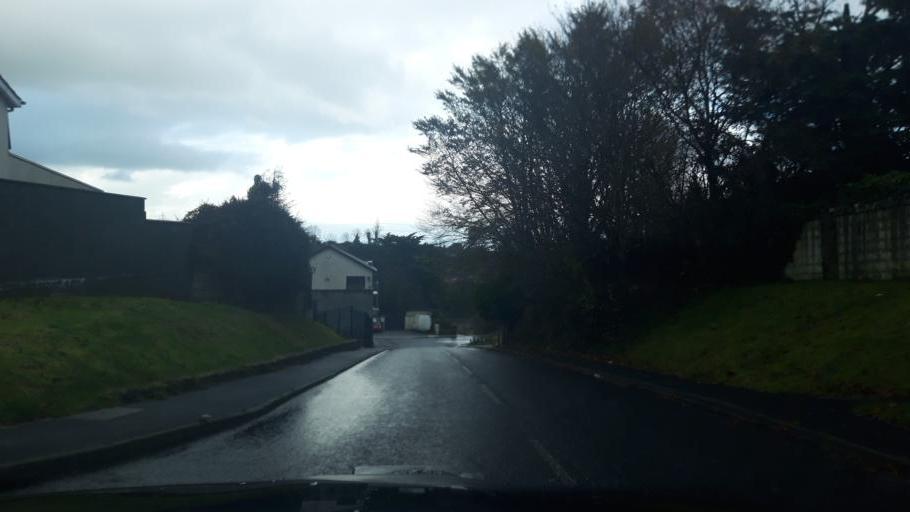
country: IE
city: Newtownmountkennedy
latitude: 53.0881
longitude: -6.1107
